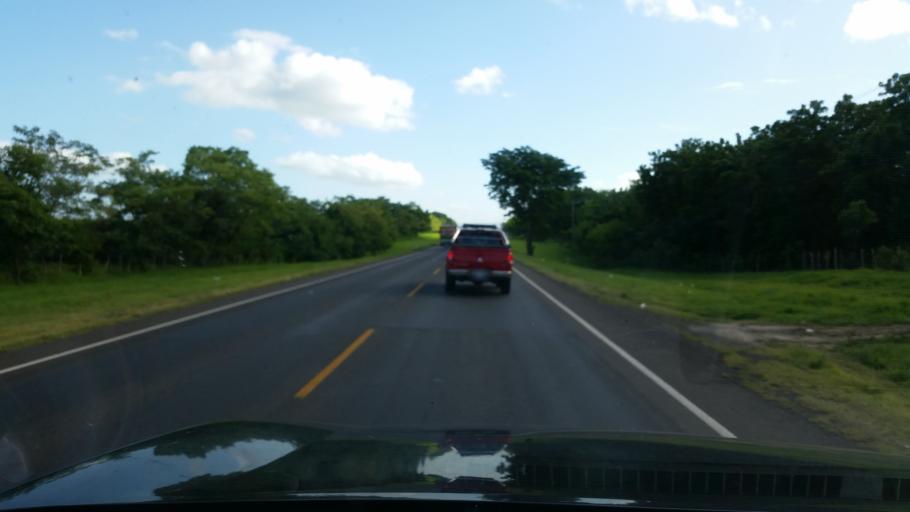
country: NI
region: Managua
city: Tipitapa
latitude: 12.3373
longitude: -86.0512
